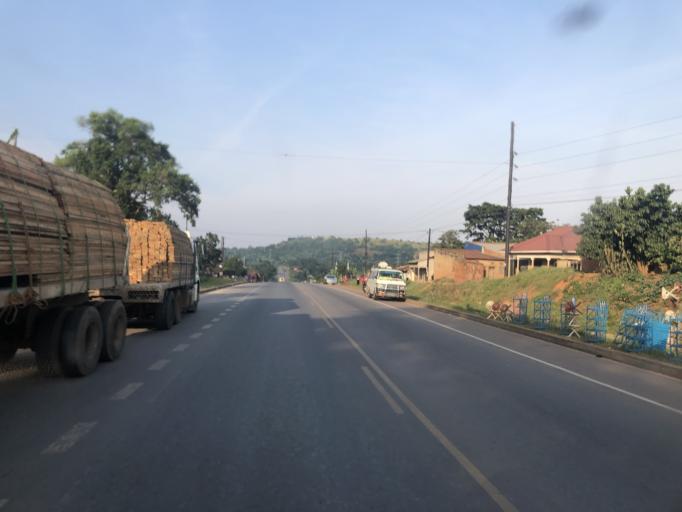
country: UG
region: Central Region
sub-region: Mpigi District
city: Mpigi
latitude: 0.1719
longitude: 32.2630
